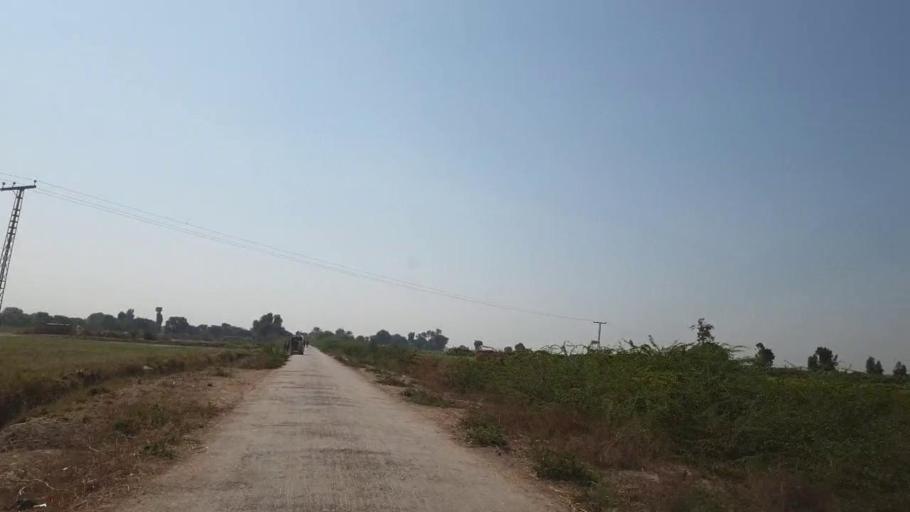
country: PK
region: Sindh
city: Kunri
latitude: 25.1660
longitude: 69.5276
